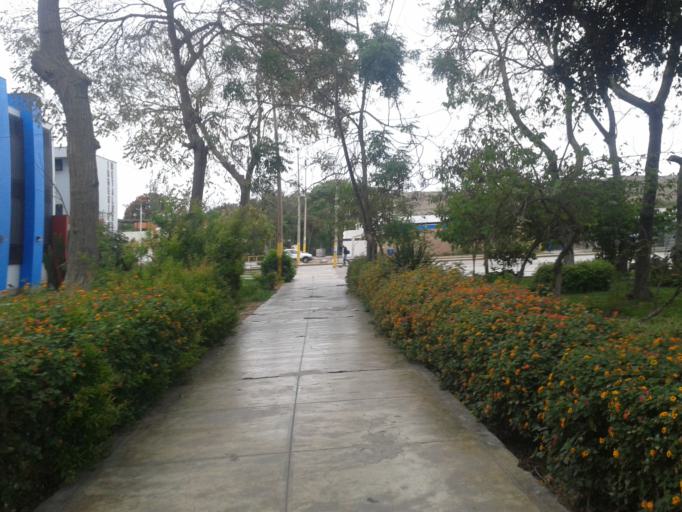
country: PE
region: Callao
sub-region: Callao
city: Callao
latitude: -12.0600
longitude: -77.0838
